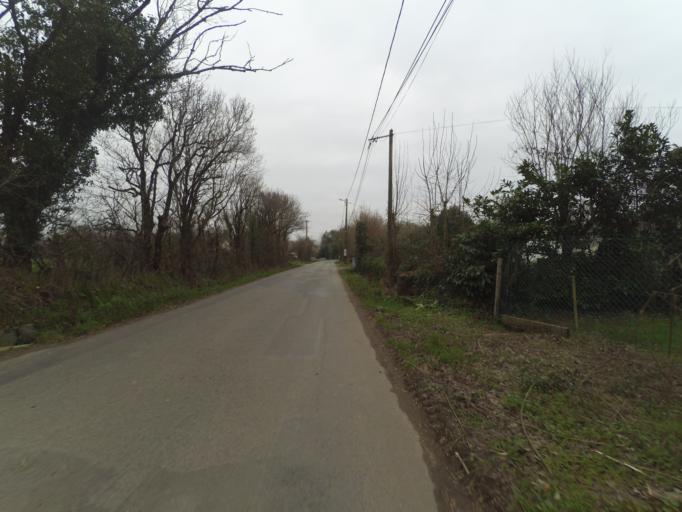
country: FR
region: Pays de la Loire
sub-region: Departement de la Loire-Atlantique
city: Coueron
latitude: 47.2307
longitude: -1.6895
